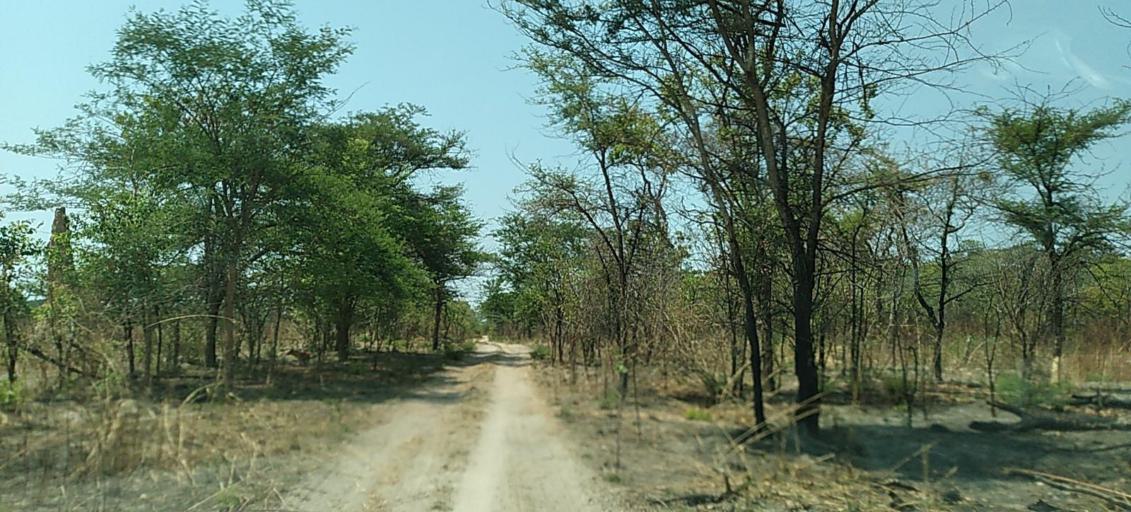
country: ZM
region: Copperbelt
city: Mpongwe
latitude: -13.8366
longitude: 28.0595
